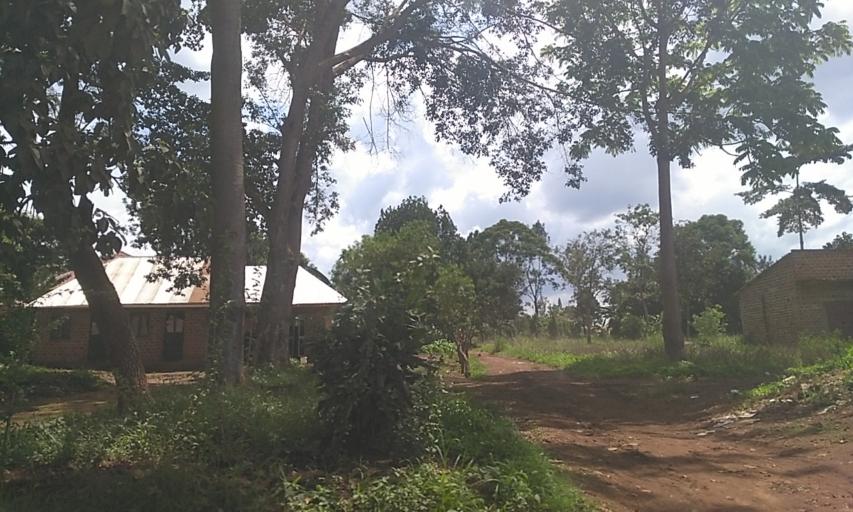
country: UG
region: Central Region
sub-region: Wakiso District
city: Wakiso
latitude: 0.3960
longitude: 32.4737
